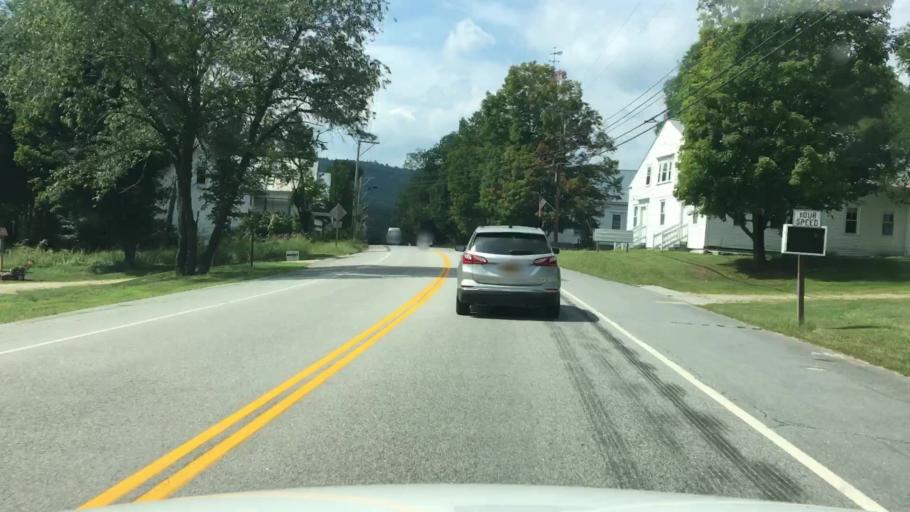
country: US
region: Maine
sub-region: Oxford County
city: Rumford
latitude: 44.5126
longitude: -70.6125
